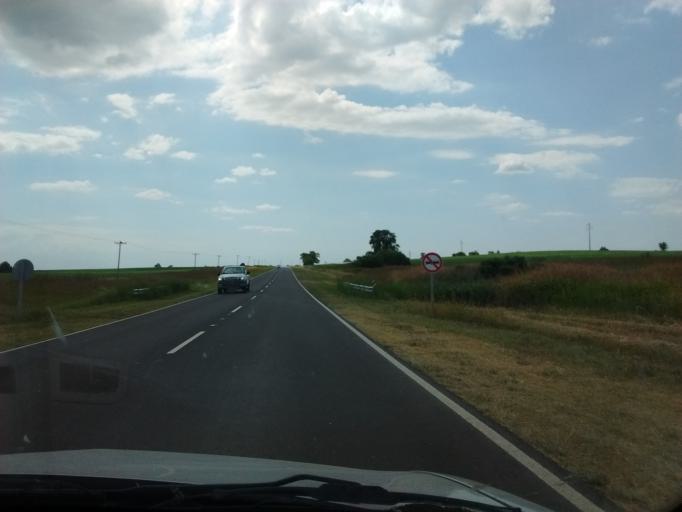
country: AR
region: Entre Rios
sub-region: Departamento de Victoria
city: Victoria
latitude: -32.6662
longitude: -60.0430
